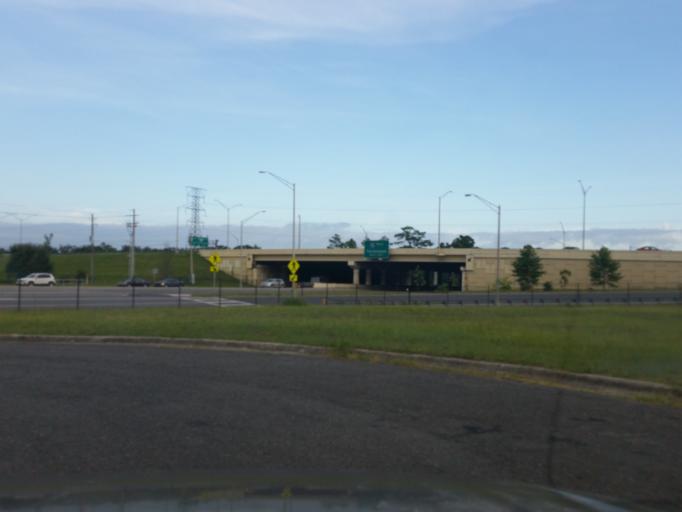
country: US
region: Florida
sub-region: Escambia County
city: Ferry Pass
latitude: 30.5050
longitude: -87.2222
